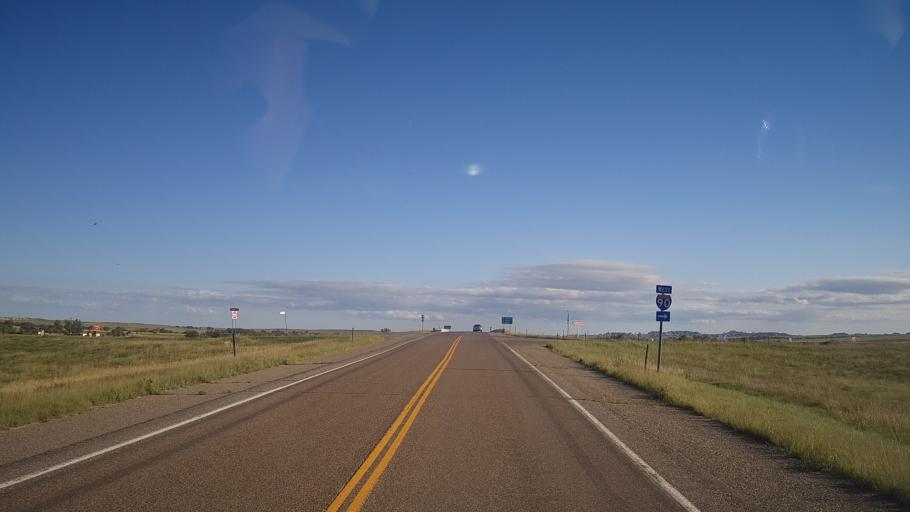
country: US
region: South Dakota
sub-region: Haakon County
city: Philip
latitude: 43.8427
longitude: -101.8997
